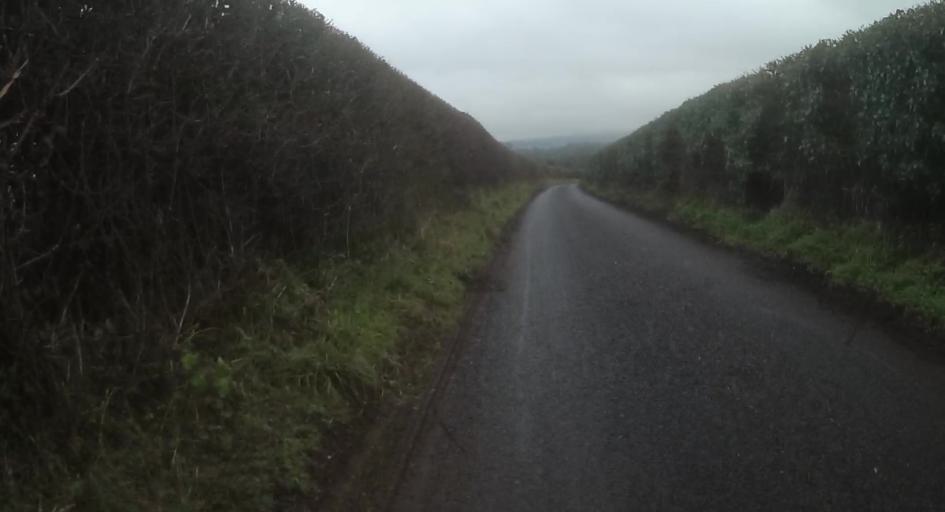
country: GB
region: England
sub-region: Hampshire
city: Kings Worthy
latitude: 51.0989
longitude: -1.2526
